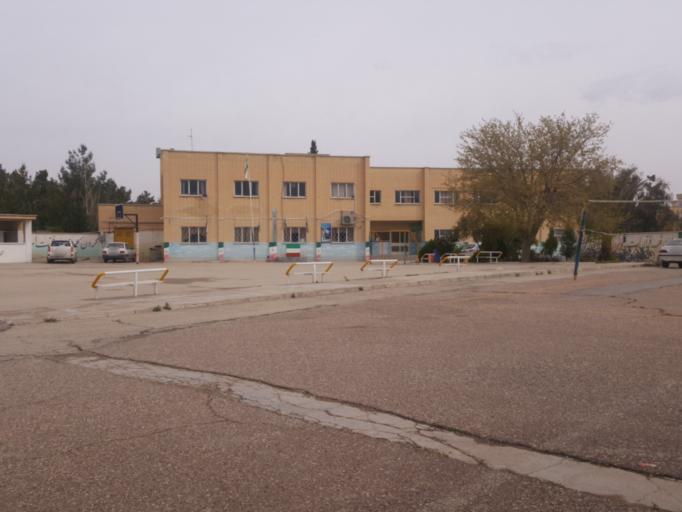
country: IR
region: Fars
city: Marvdasht
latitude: 29.8778
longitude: 52.8239
